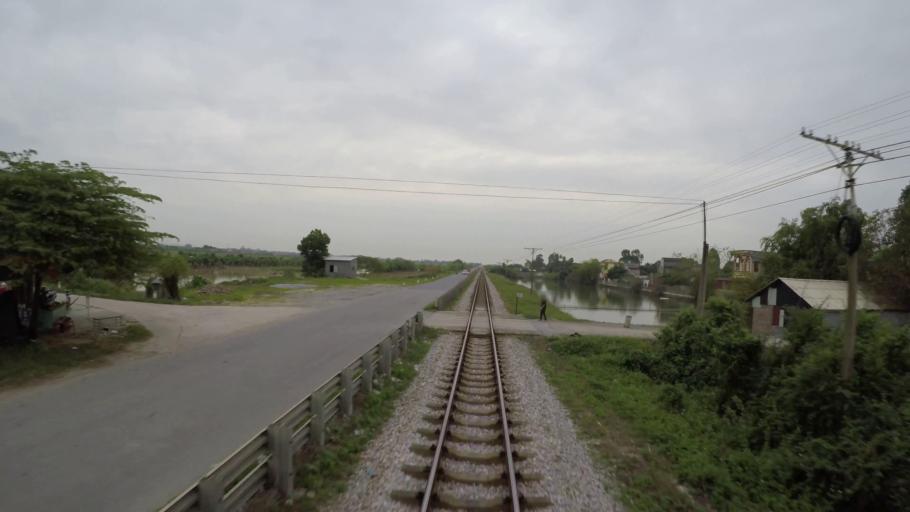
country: VN
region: Hung Yen
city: Ban Yen Nhan
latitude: 20.9803
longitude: 106.0806
